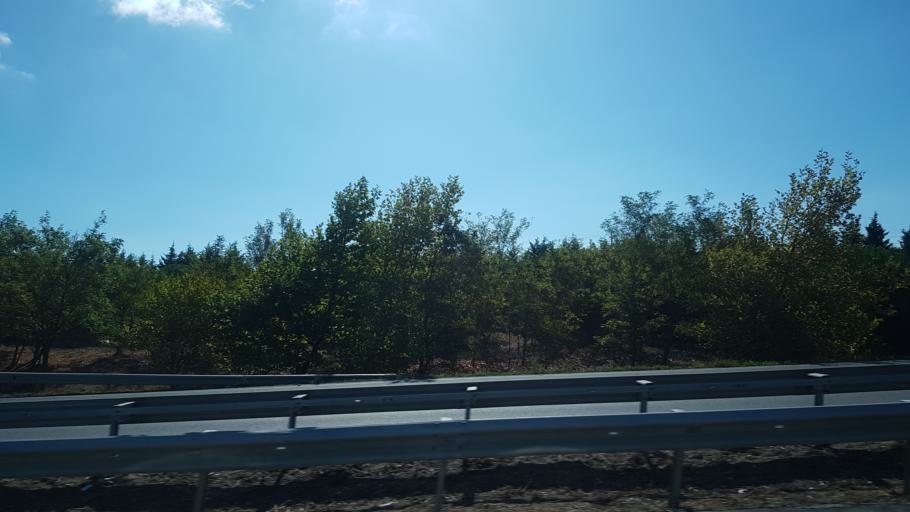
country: TR
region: Istanbul
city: Canta
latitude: 41.0787
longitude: 28.1263
